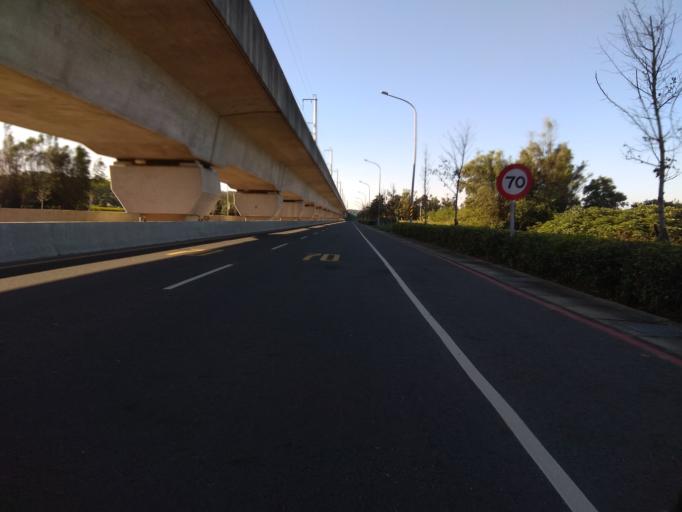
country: TW
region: Taiwan
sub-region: Hsinchu
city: Zhubei
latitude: 24.8960
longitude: 121.0785
